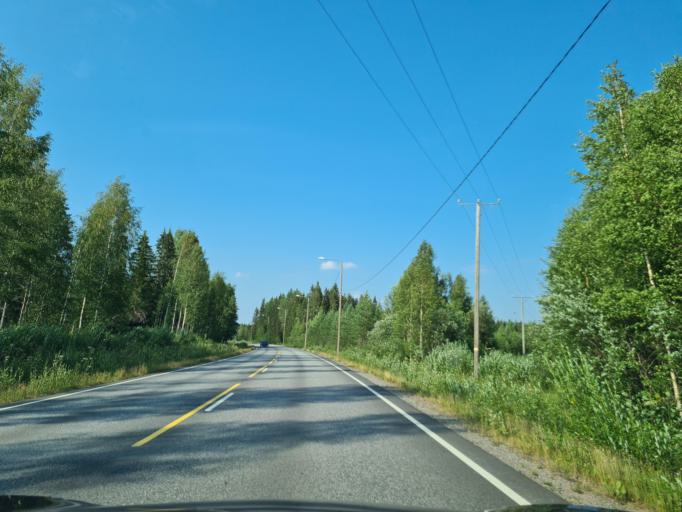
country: FI
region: Satakunta
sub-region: Pohjois-Satakunta
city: Karvia
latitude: 62.0841
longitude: 22.5259
